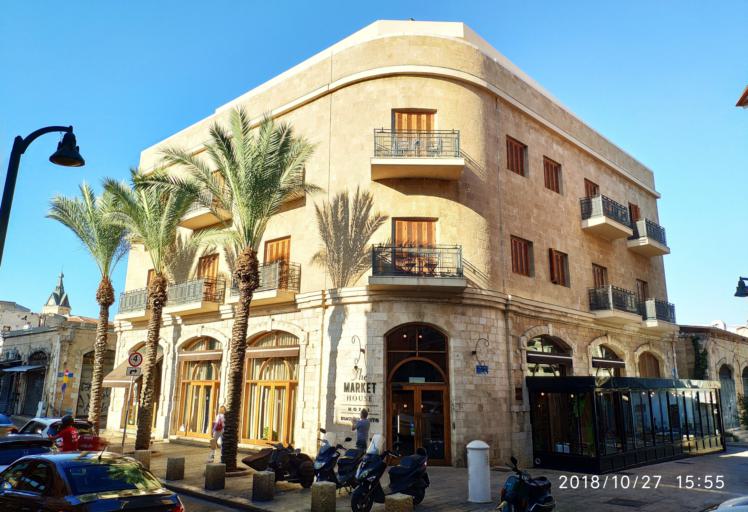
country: IL
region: Tel Aviv
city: Yafo
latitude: 32.0538
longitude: 34.7569
